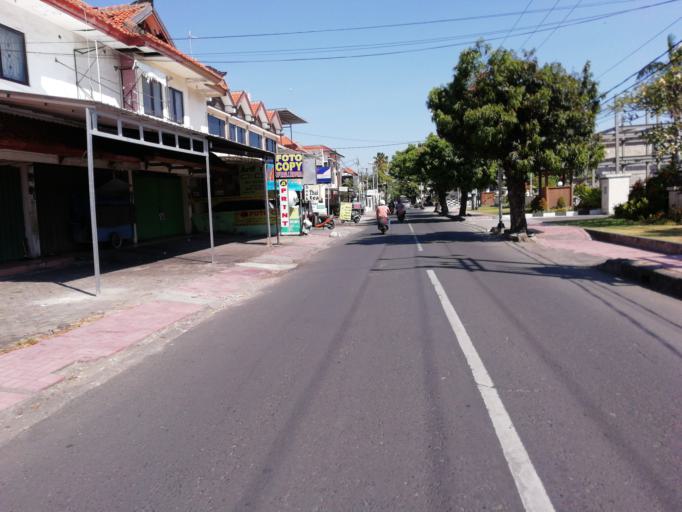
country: ID
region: Bali
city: Karyadharma
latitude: -8.6960
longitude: 115.2270
